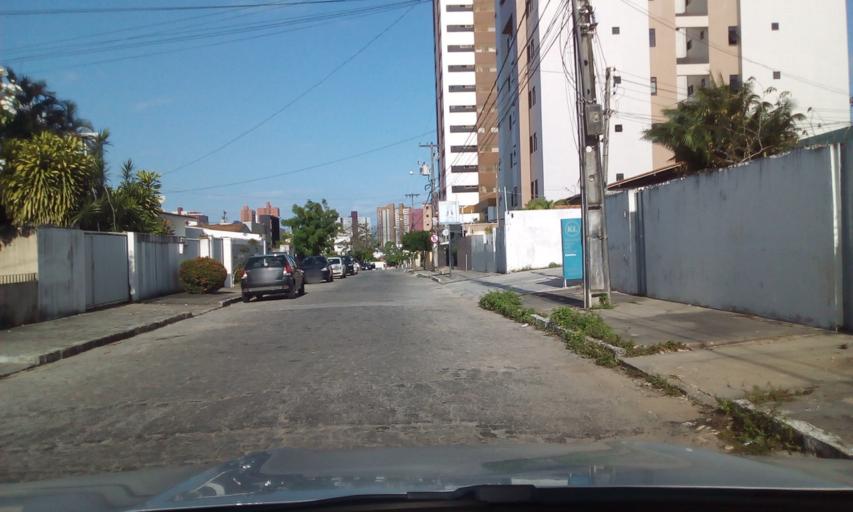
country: BR
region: Paraiba
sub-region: Joao Pessoa
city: Joao Pessoa
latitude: -7.1204
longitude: -34.8420
